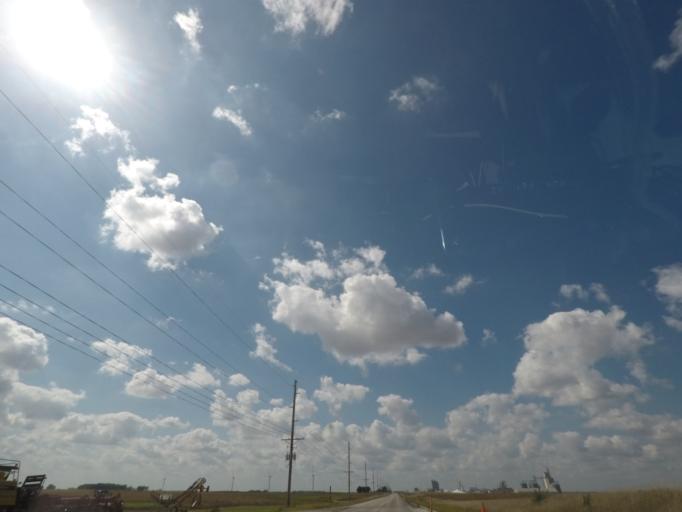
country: US
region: Iowa
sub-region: Story County
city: Nevada
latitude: 42.0230
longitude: -93.4865
